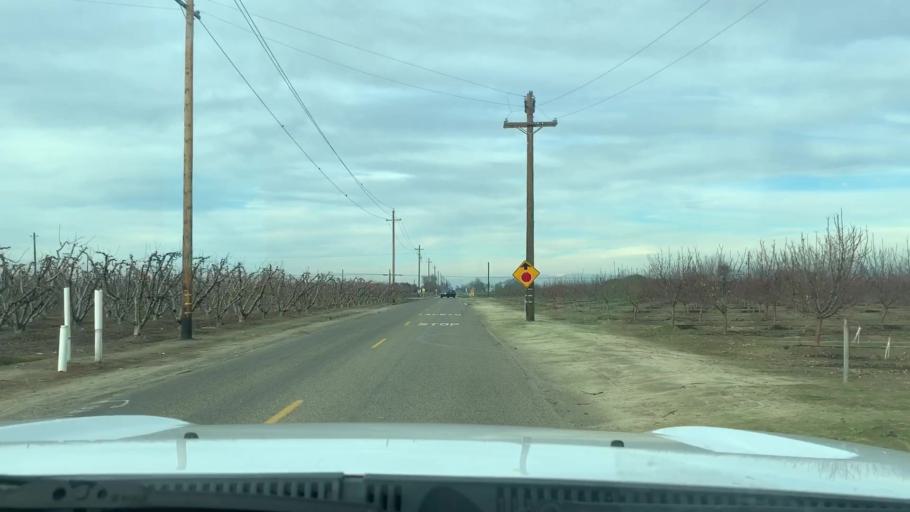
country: US
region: California
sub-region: Fresno County
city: Selma
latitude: 36.5889
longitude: -119.5749
